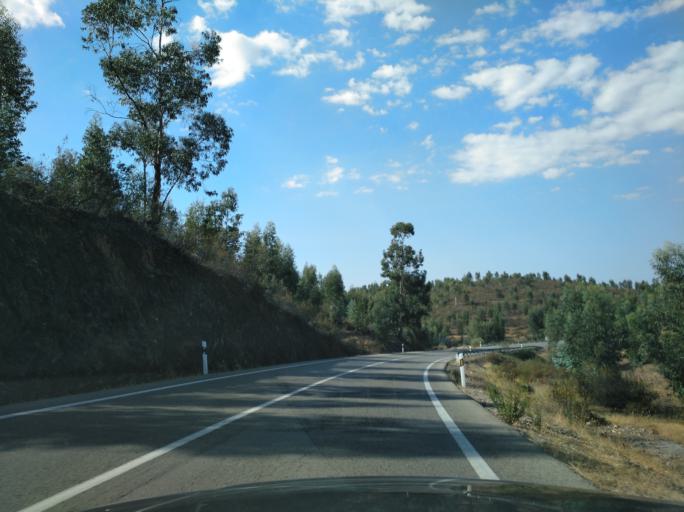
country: ES
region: Andalusia
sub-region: Provincia de Huelva
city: Santa Barbara de Casa
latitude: 37.8149
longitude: -7.2109
